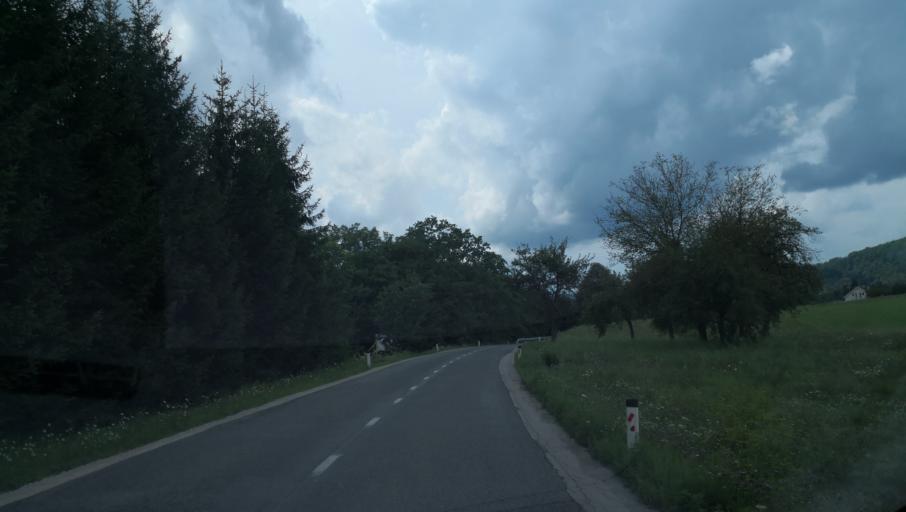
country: SI
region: Ivancna Gorica
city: Ivancna Gorica
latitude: 45.8635
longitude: 14.8284
